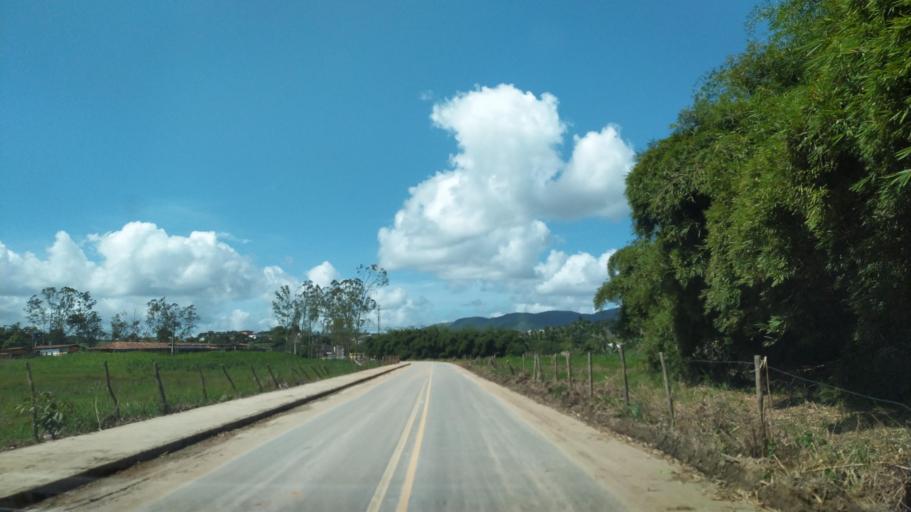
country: BR
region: Alagoas
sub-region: Uniao Dos Palmares
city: Uniao dos Palmares
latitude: -9.1568
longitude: -36.0397
